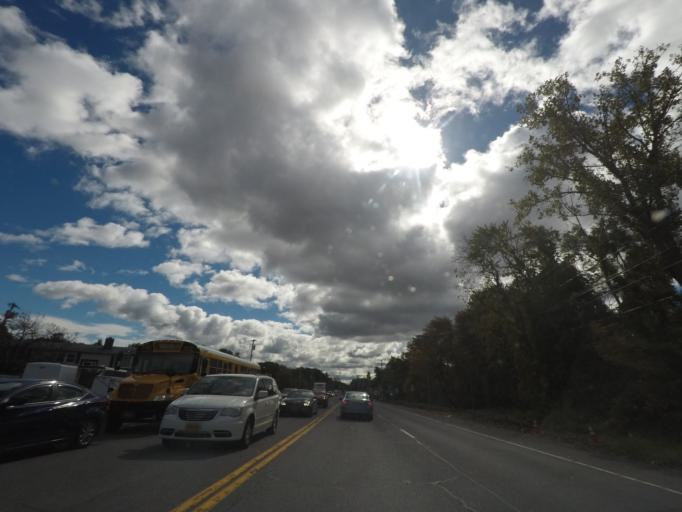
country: US
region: New York
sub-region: Saratoga County
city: Waterford
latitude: 42.8372
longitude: -73.7417
